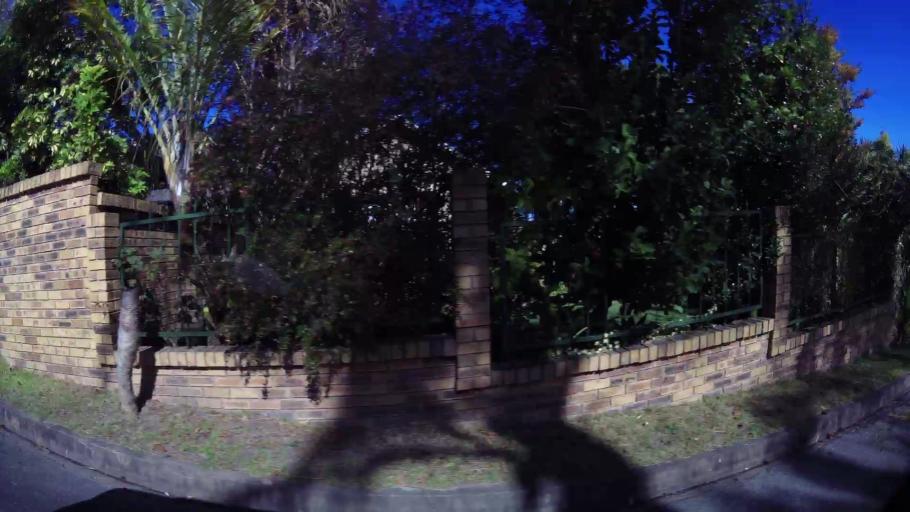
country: ZA
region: Western Cape
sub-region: Eden District Municipality
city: George
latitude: -33.9471
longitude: 22.4613
